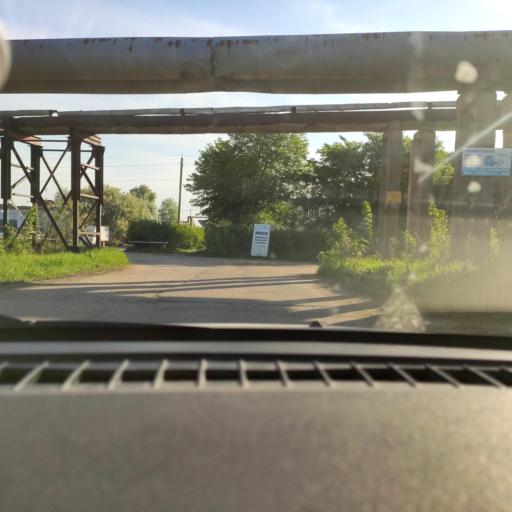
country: RU
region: Perm
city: Kondratovo
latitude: 57.9903
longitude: 56.1102
